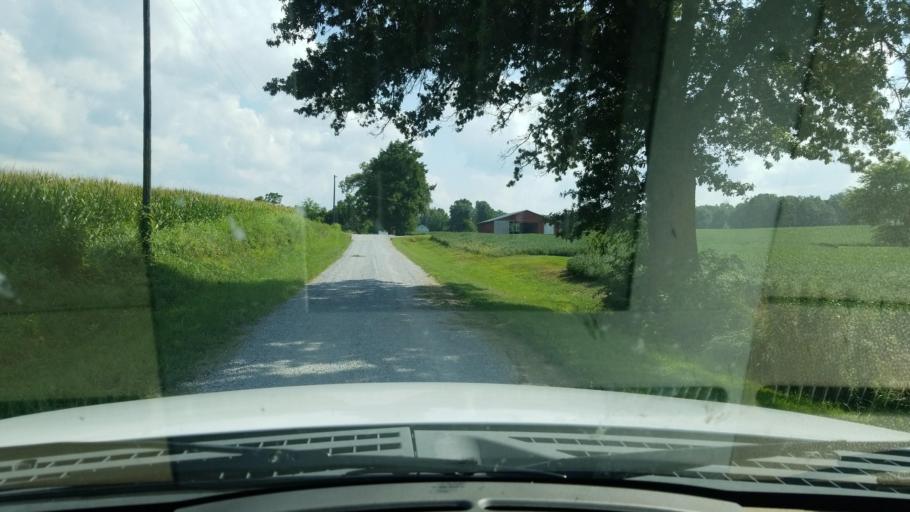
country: US
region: Illinois
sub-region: Saline County
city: Eldorado
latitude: 37.8441
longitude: -88.4802
